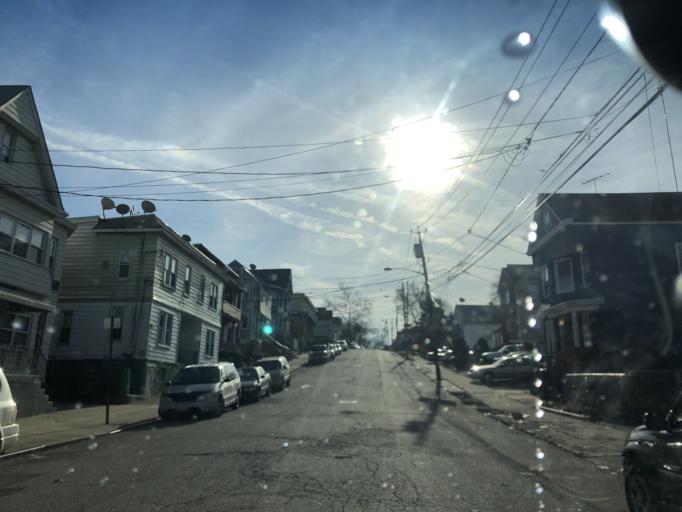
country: US
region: New Jersey
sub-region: Passaic County
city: Hawthorne
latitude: 40.9366
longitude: -74.1462
